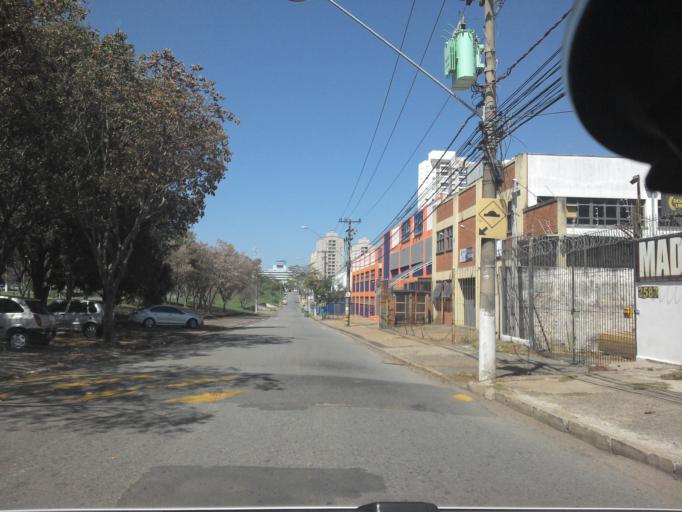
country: BR
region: Sao Paulo
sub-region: Campinas
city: Campinas
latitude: -22.8503
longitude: -47.0428
